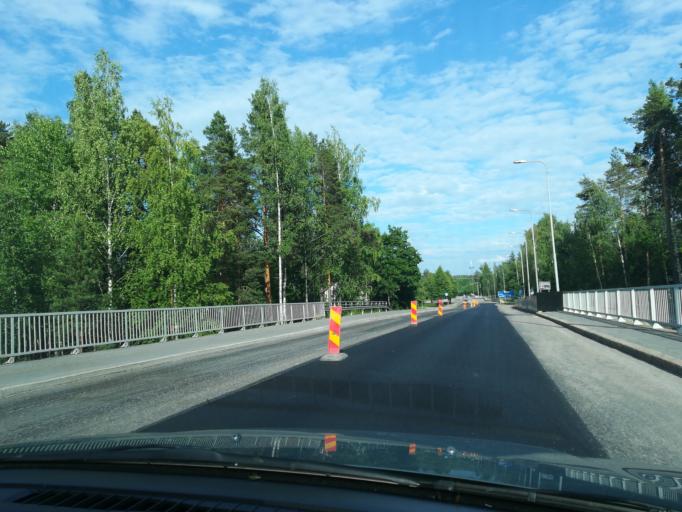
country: FI
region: South Karelia
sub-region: Imatra
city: Imatra
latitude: 61.1665
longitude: 28.7857
